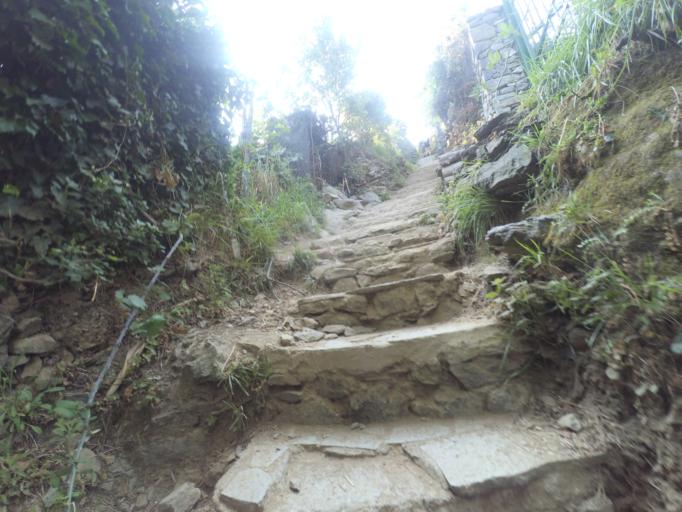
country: IT
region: Liguria
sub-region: Provincia di La Spezia
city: Monterosso al Mare
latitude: 44.1450
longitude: 9.6620
